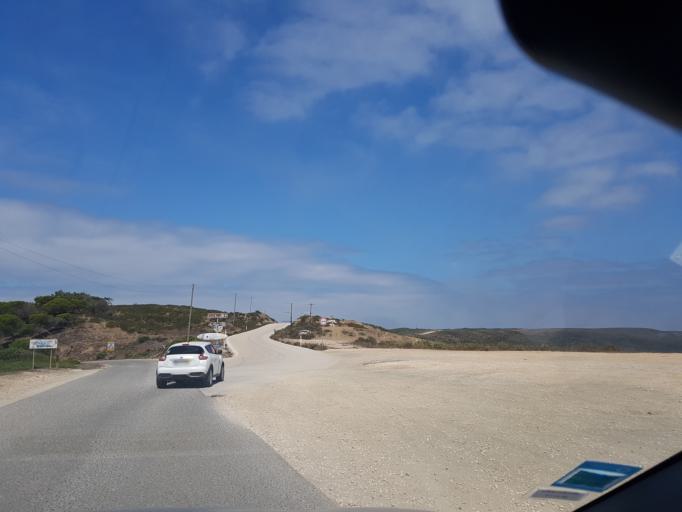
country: PT
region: Faro
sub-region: Vila do Bispo
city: Vila do Bispo
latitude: 37.0959
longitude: -8.9344
